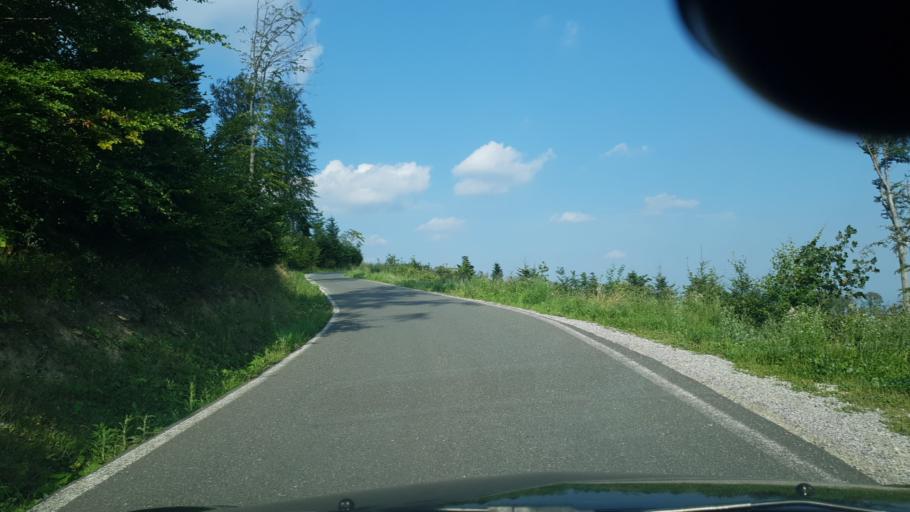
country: HR
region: Grad Zagreb
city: Kasina
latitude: 45.8907
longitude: 15.9567
